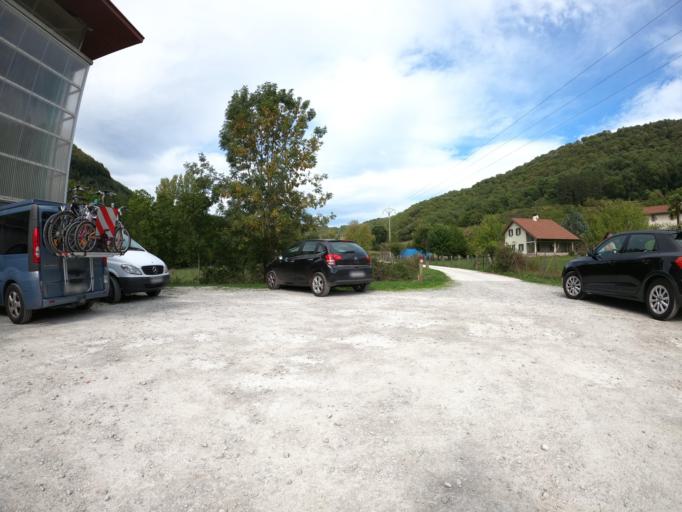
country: ES
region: Navarre
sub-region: Provincia de Navarra
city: Irurtzun
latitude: 42.9559
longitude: -1.8239
